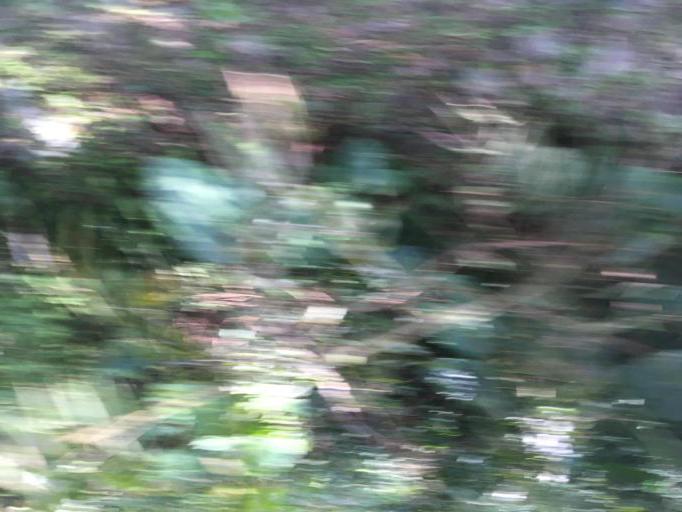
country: TW
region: Taiwan
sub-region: Yilan
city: Yilan
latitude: 24.7564
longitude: 121.6136
